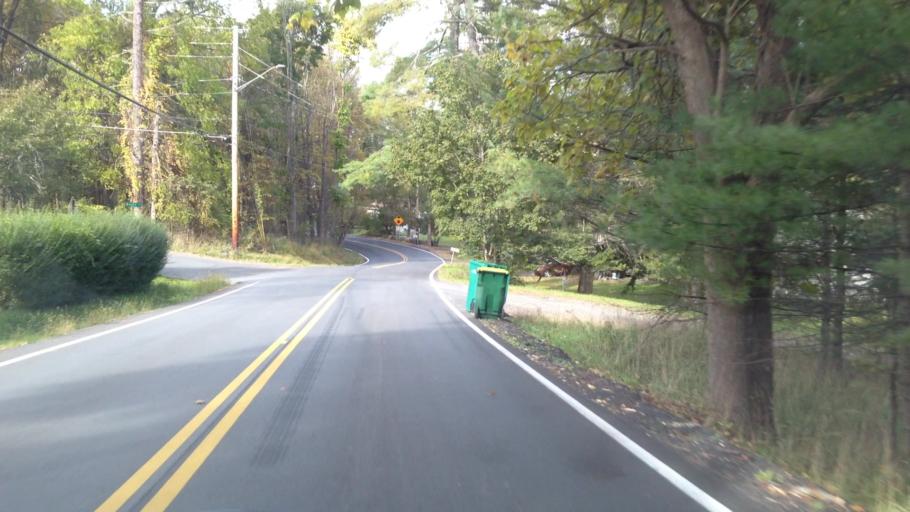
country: US
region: New York
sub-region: Ulster County
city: Tillson
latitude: 41.8372
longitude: -74.0377
